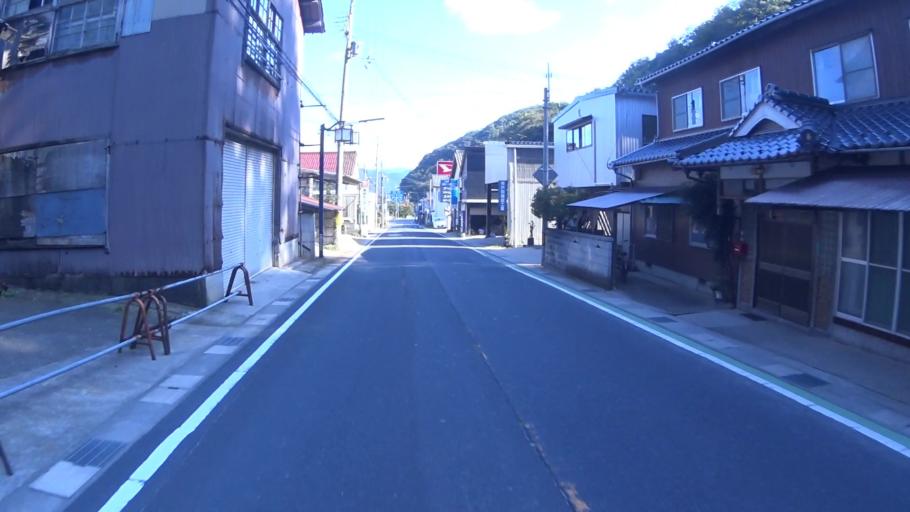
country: JP
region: Kyoto
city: Miyazu
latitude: 35.7326
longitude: 135.0943
